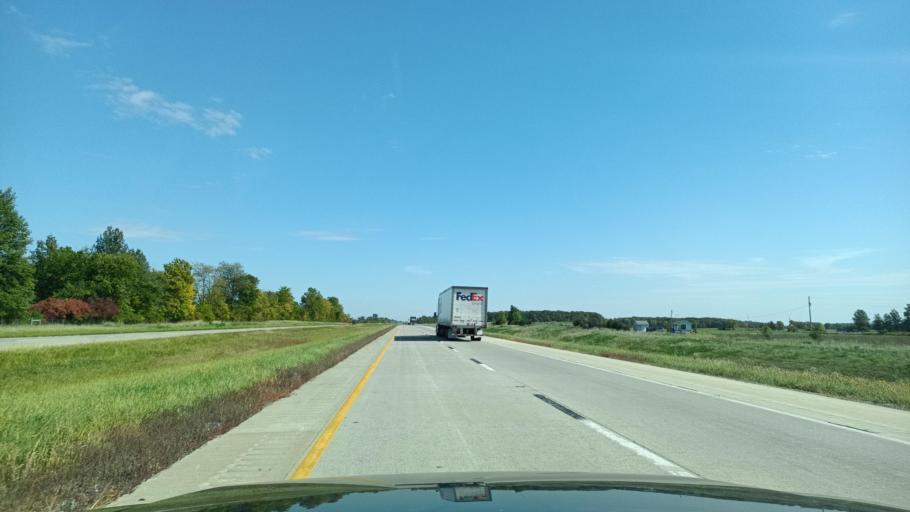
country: US
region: Ohio
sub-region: Paulding County
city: Antwerp
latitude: 41.1969
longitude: -84.6772
